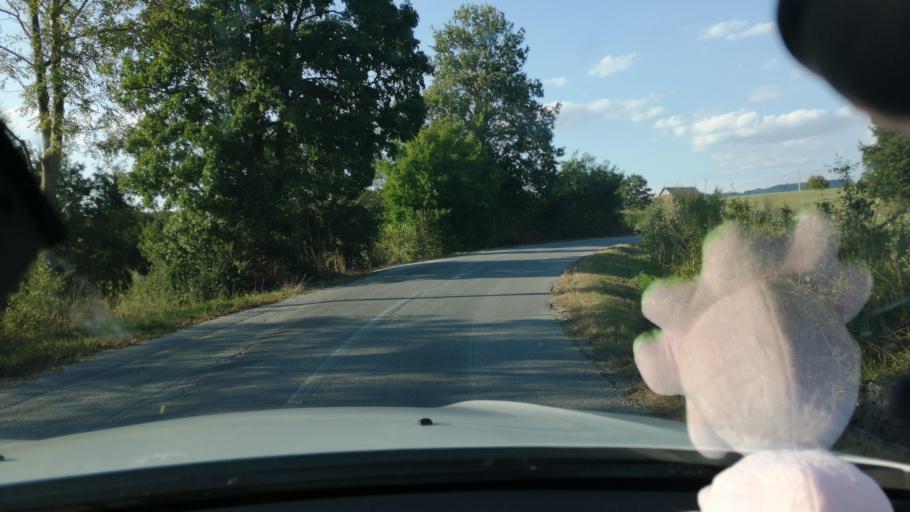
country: RS
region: Central Serbia
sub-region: Moravicki Okrug
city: Lucani
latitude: 43.8107
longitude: 20.2527
